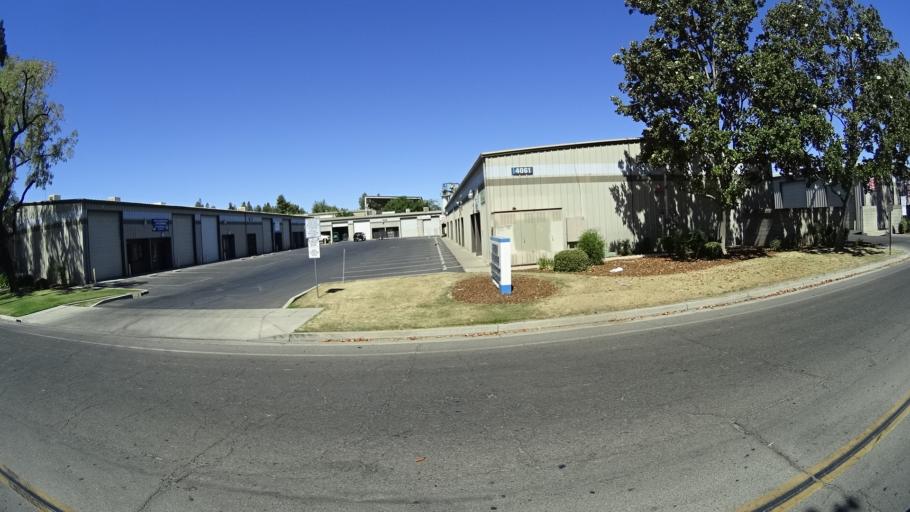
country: US
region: California
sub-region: Fresno County
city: West Park
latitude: 36.7951
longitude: -119.8533
